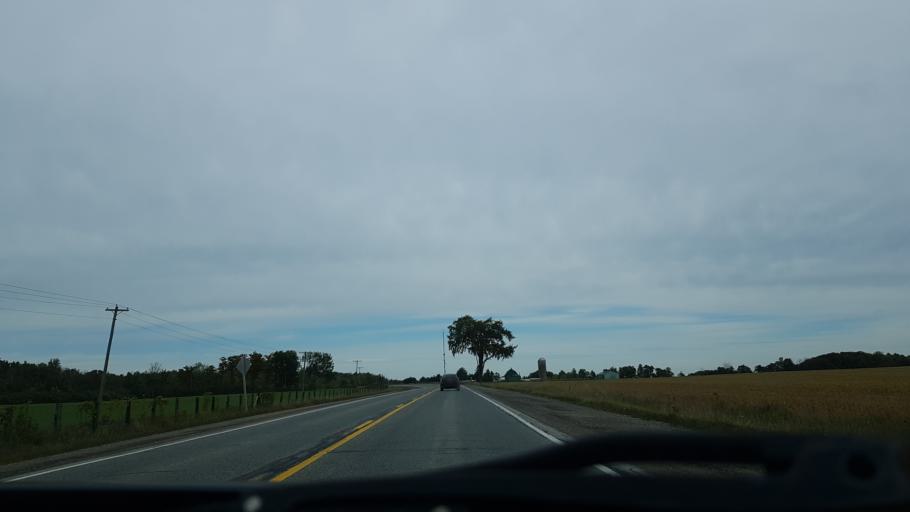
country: CA
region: Ontario
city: Orangeville
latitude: 43.9002
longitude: -79.9507
